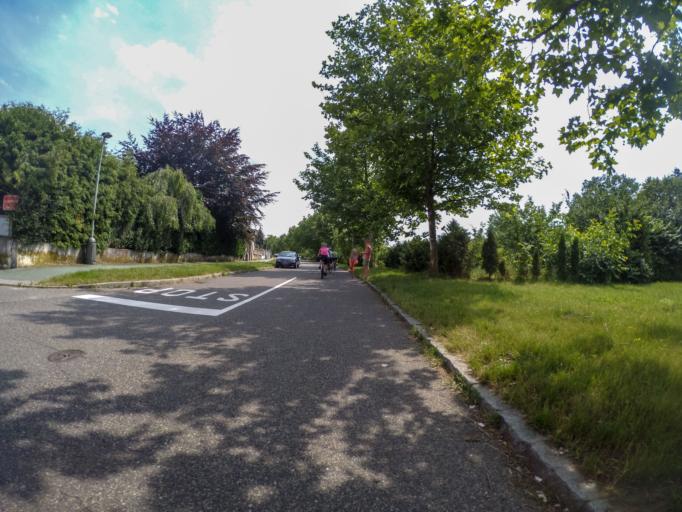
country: CZ
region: Praha
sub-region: Praha 19
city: Kbely
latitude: 50.1307
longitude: 14.5550
